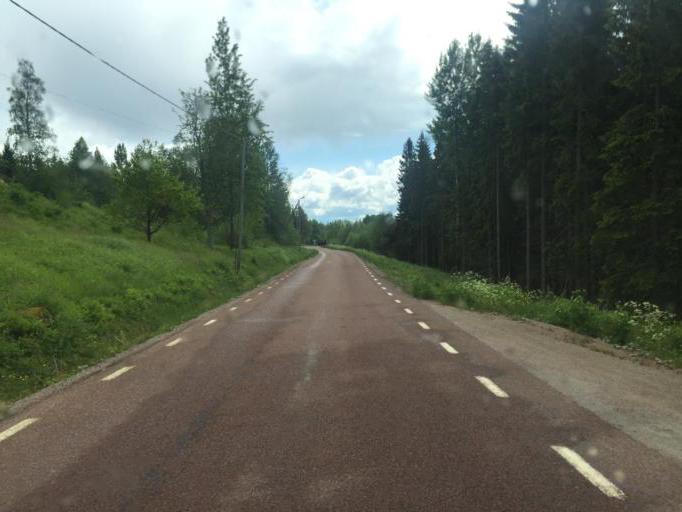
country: SE
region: Dalarna
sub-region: Malung-Saelens kommun
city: Malung
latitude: 60.3714
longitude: 13.8711
